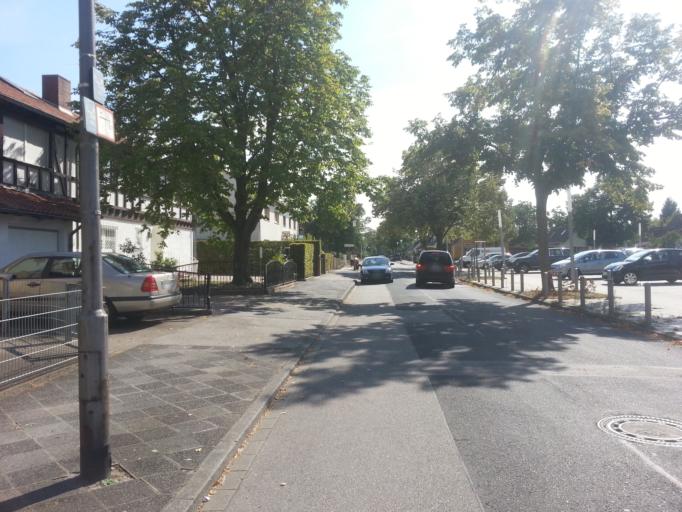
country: DE
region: Baden-Wuerttemberg
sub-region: Karlsruhe Region
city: Mannheim
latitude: 49.5433
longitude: 8.4778
